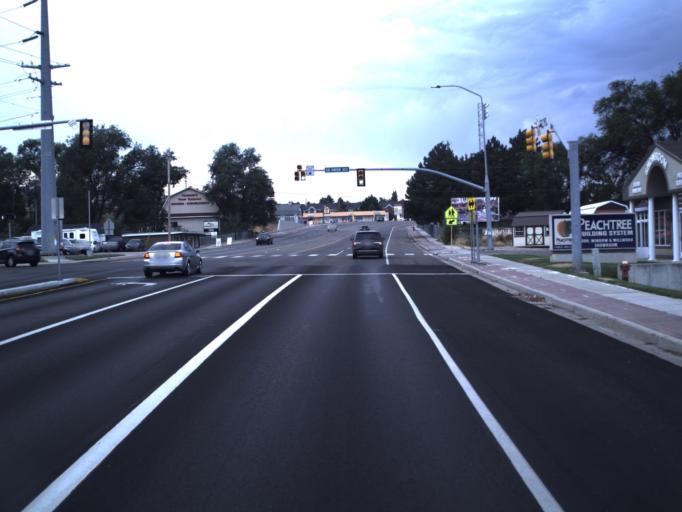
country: US
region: Utah
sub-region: Salt Lake County
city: Sandy City
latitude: 40.6205
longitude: -111.8661
